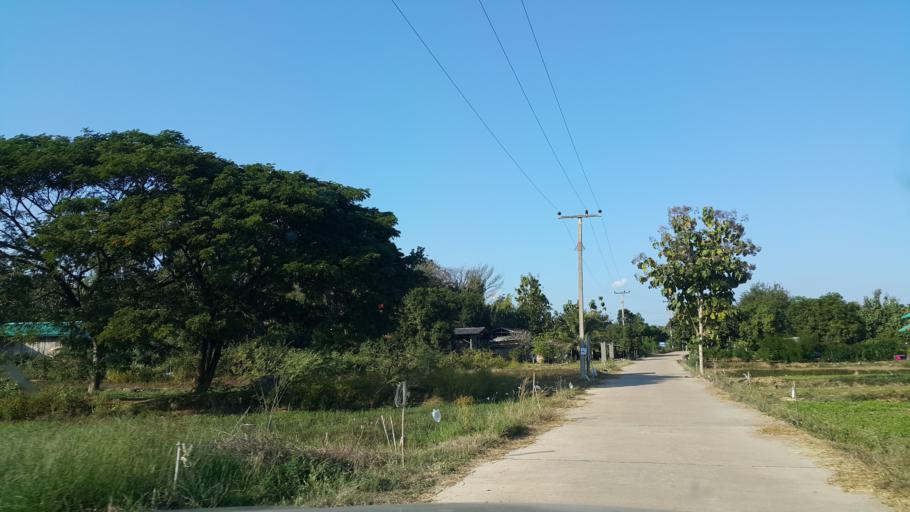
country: TH
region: Sukhothai
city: Thung Saliam
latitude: 17.3775
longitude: 99.5218
